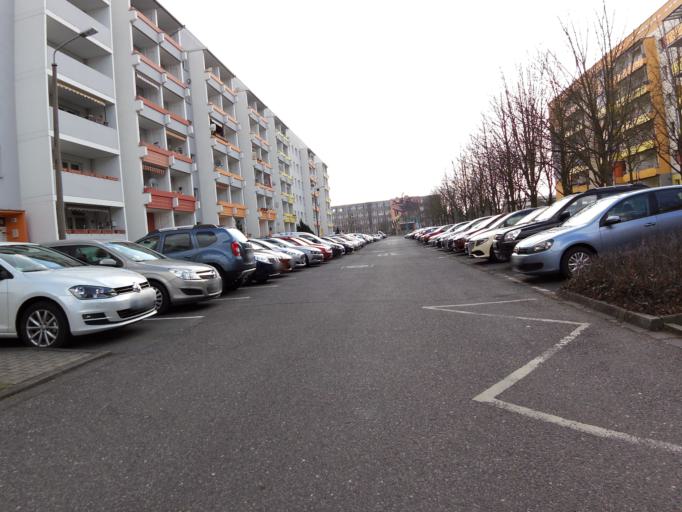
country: DE
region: Saxony
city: Markranstadt
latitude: 51.3065
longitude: 12.2671
